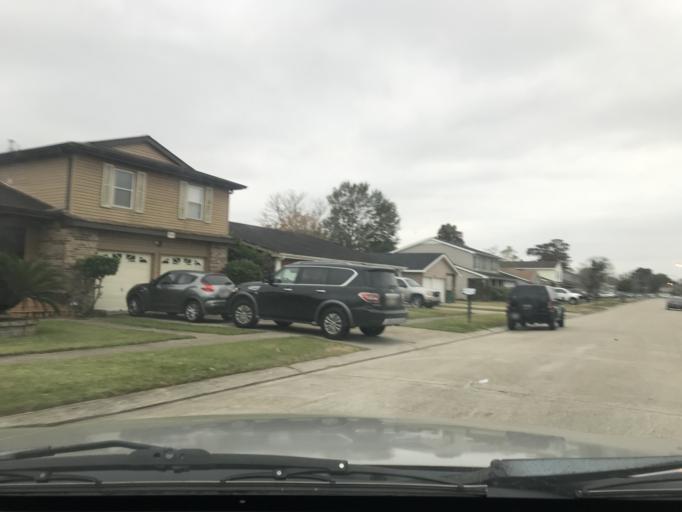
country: US
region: Louisiana
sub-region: Jefferson Parish
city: Woodmere
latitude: 29.8631
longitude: -90.0755
